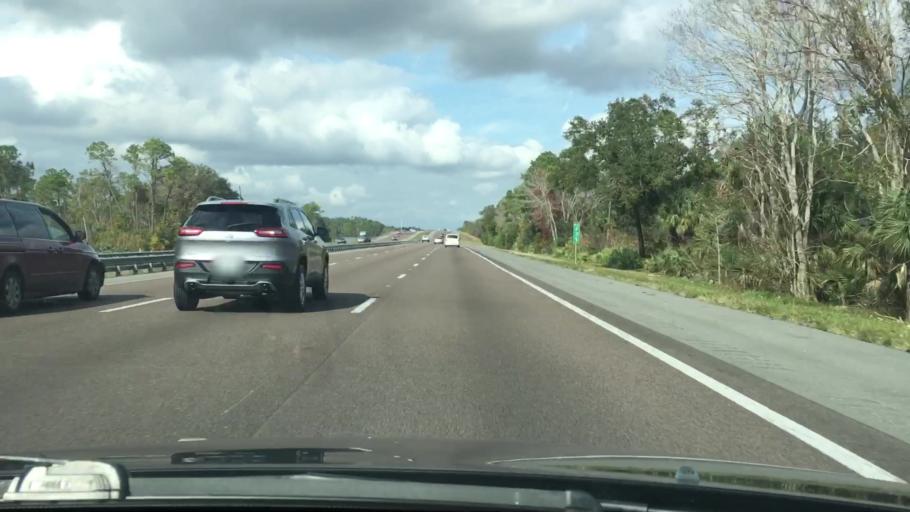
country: US
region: Florida
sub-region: Volusia County
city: Oak Hill
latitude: 28.8263
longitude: -80.9097
